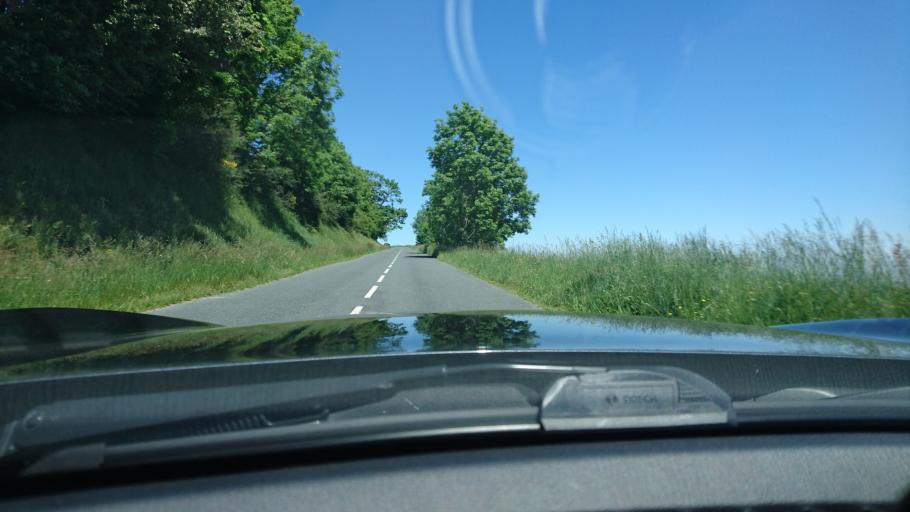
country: FR
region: Rhone-Alpes
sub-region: Departement du Rhone
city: Courzieu
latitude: 45.7229
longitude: 4.5960
